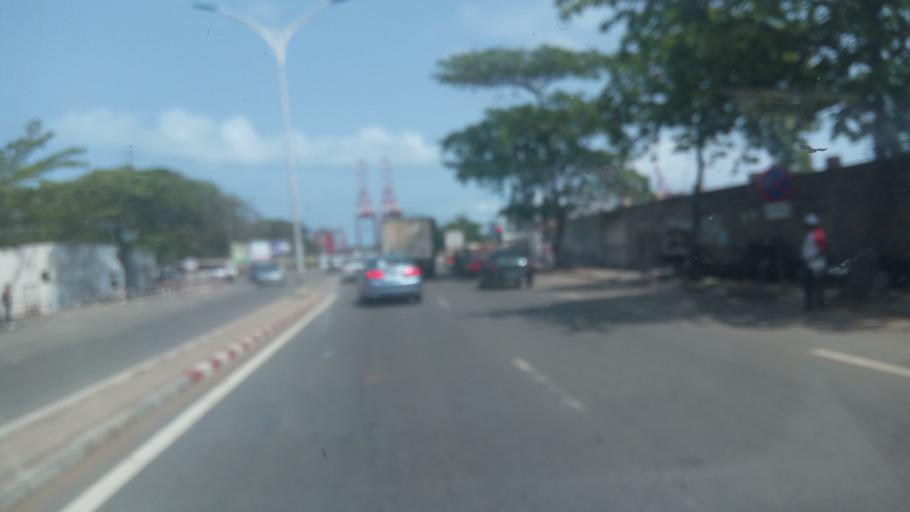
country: TG
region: Maritime
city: Lome
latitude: 6.1520
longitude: 1.2863
